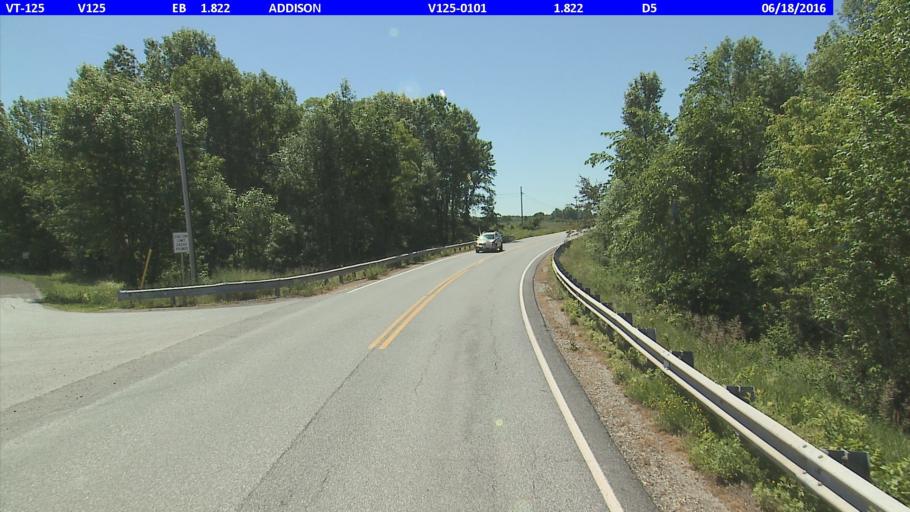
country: US
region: New York
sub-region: Essex County
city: Port Henry
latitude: 44.0225
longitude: -73.3908
